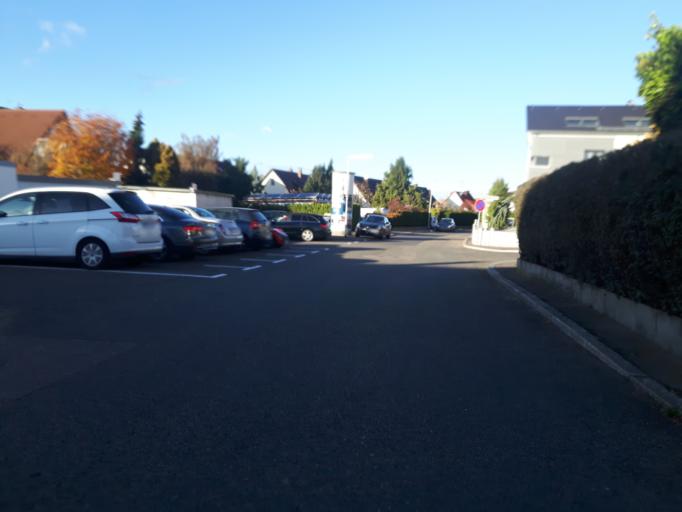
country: DE
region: Baden-Wuerttemberg
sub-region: Regierungsbezirk Stuttgart
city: Heilbronn
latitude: 49.1607
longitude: 9.2282
